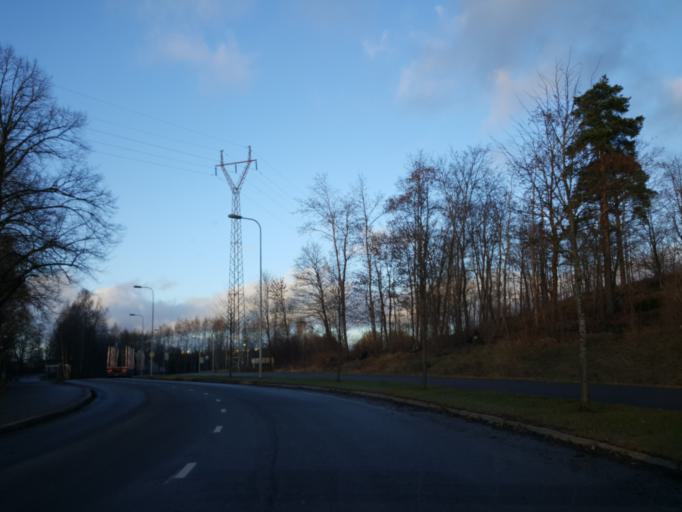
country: FI
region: Uusimaa
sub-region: Helsinki
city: Lohja
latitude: 60.2568
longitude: 24.0602
